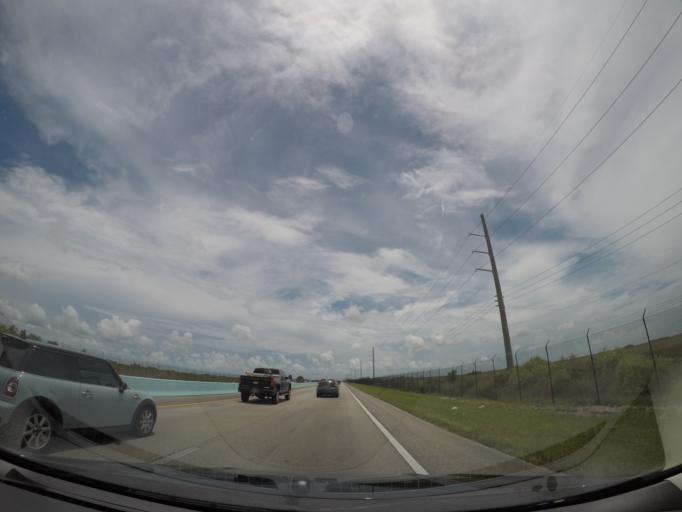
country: US
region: Florida
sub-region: Miami-Dade County
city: Florida City
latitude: 25.3464
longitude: -80.4572
